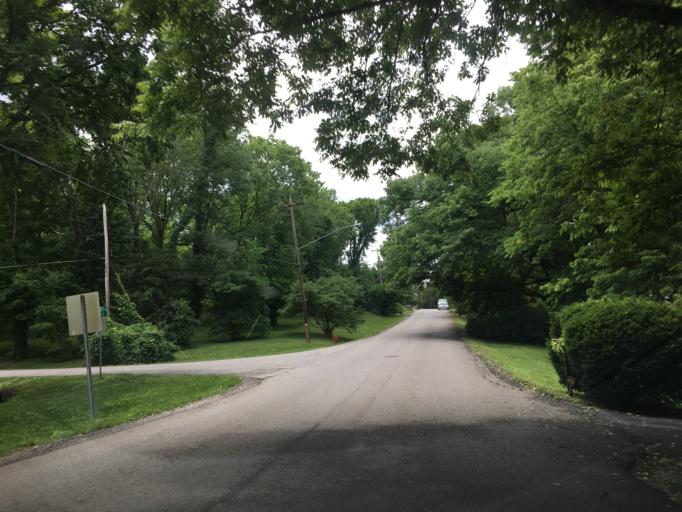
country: US
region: Tennessee
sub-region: Davidson County
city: Belle Meade
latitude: 36.0954
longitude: -86.8303
